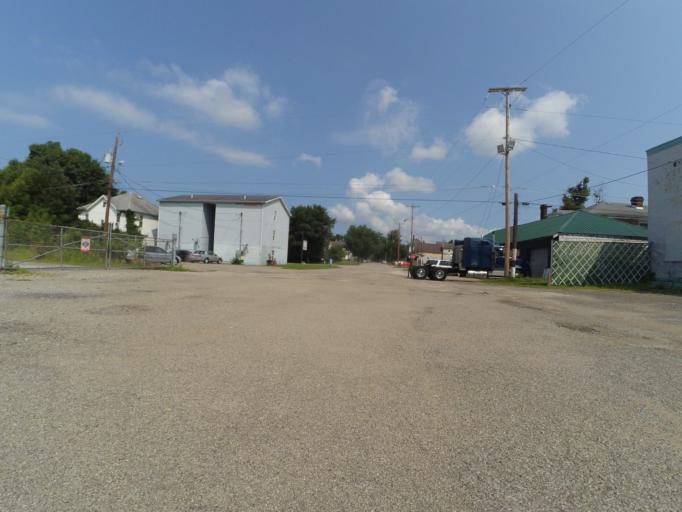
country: US
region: West Virginia
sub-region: Cabell County
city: Huntington
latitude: 38.4179
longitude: -82.4323
